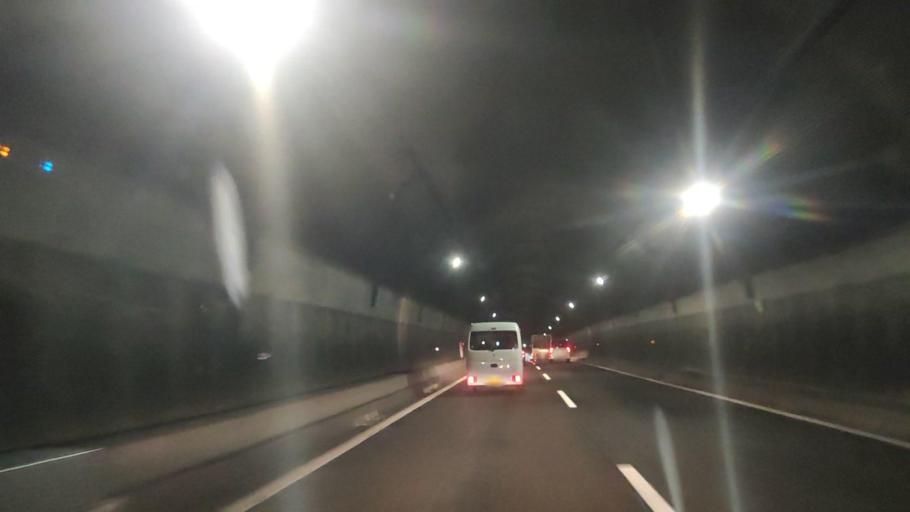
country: JP
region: Nagasaki
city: Obita
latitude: 32.8129
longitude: 129.9404
